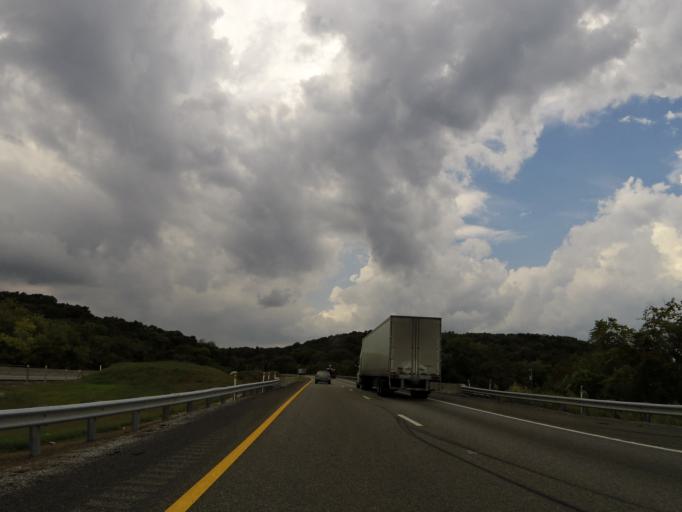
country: US
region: Tennessee
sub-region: Wilson County
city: Watertown
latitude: 36.1746
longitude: -86.0716
